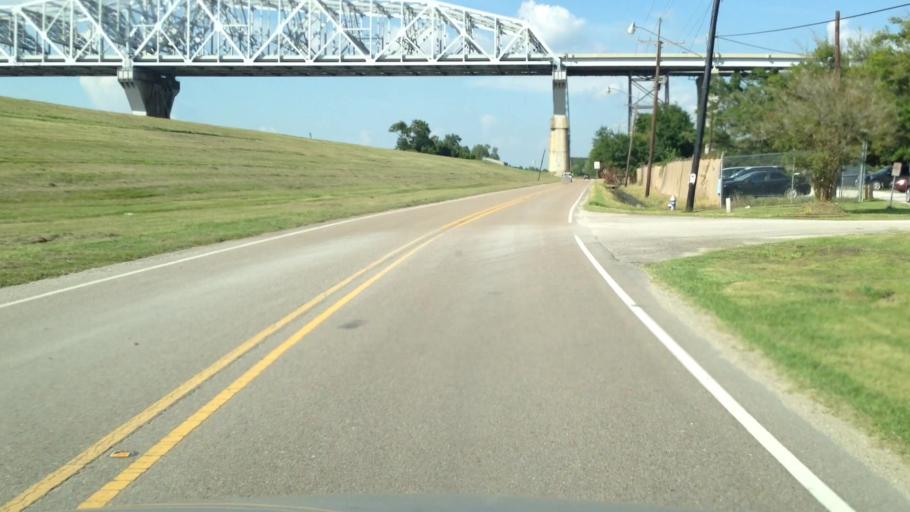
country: US
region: Louisiana
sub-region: Jefferson Parish
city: Bridge City
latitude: 29.9386
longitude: -90.1679
